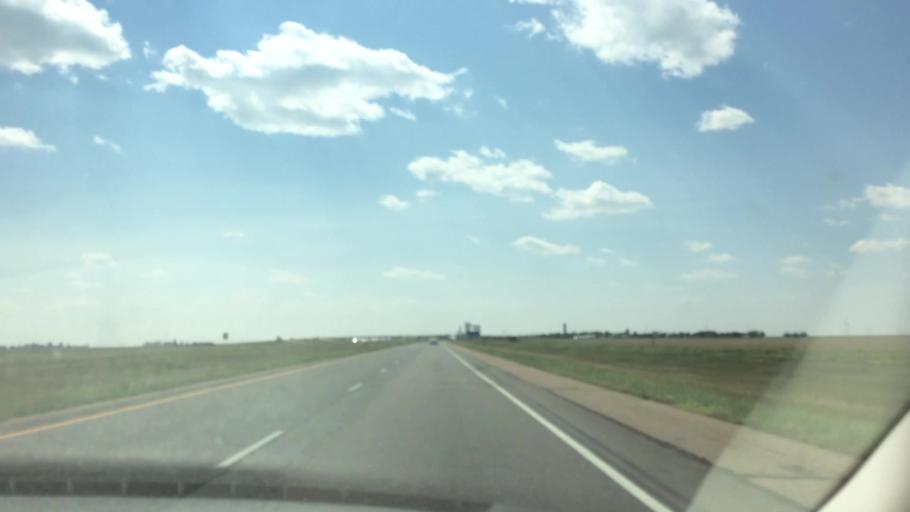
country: US
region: Colorado
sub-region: Lincoln County
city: Hugo
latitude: 39.2842
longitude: -103.2507
